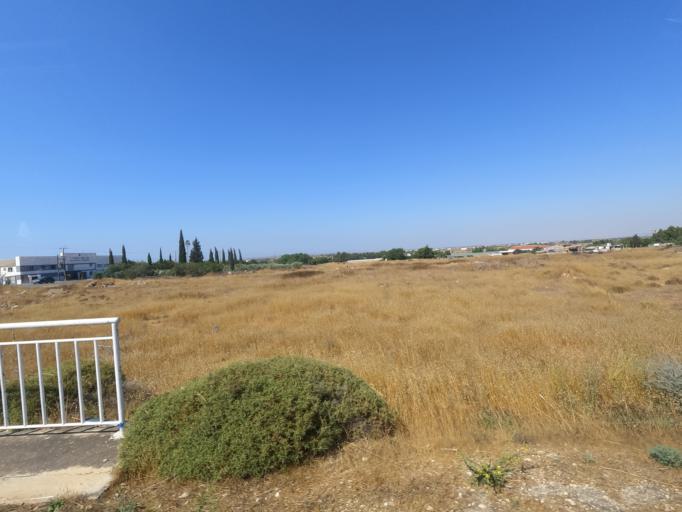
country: CY
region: Ammochostos
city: Frenaros
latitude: 35.0231
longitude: 33.9287
